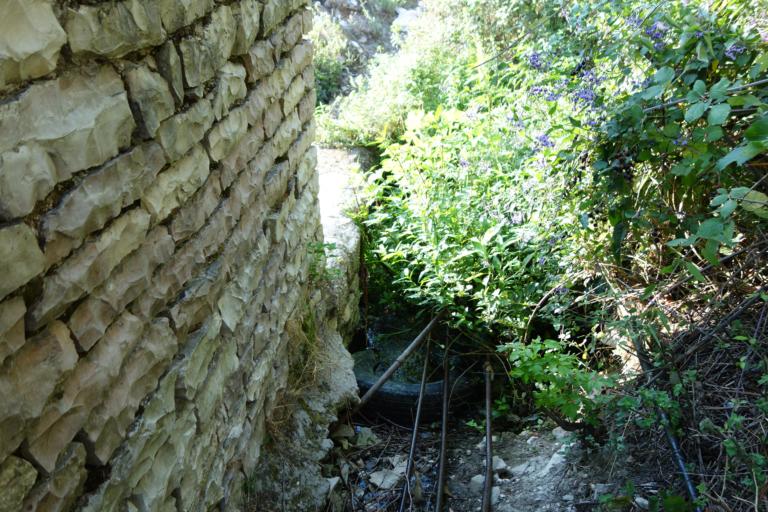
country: AL
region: Gjirokaster
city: Gjirokaster
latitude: 40.0786
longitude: 20.1444
